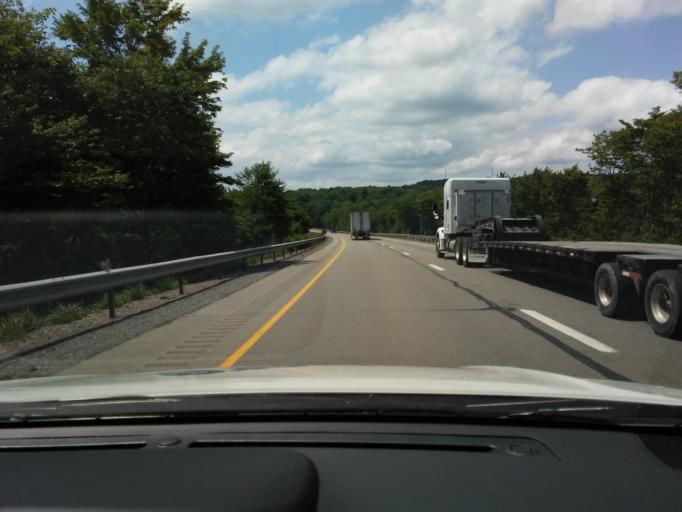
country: US
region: Pennsylvania
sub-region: Jefferson County
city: Brookville
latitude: 41.1783
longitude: -79.1217
